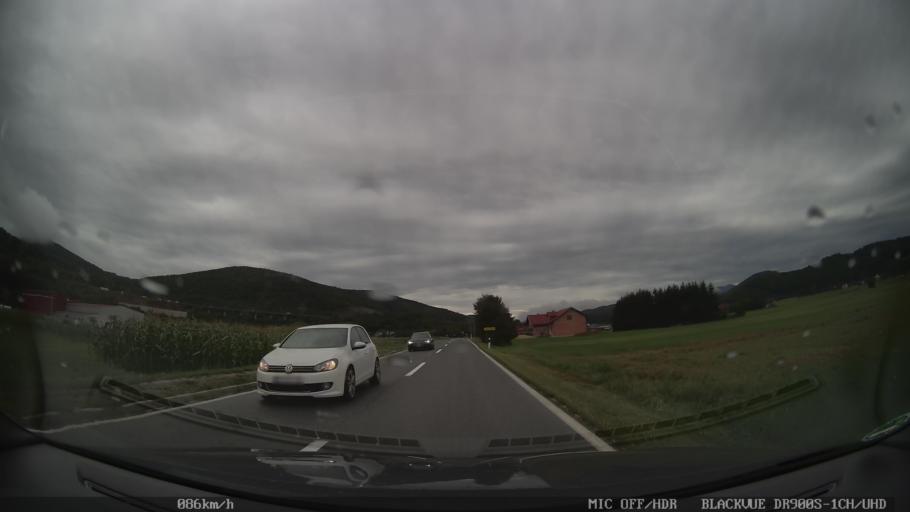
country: HR
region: Licko-Senjska
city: Otocac
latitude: 44.9094
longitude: 15.1667
